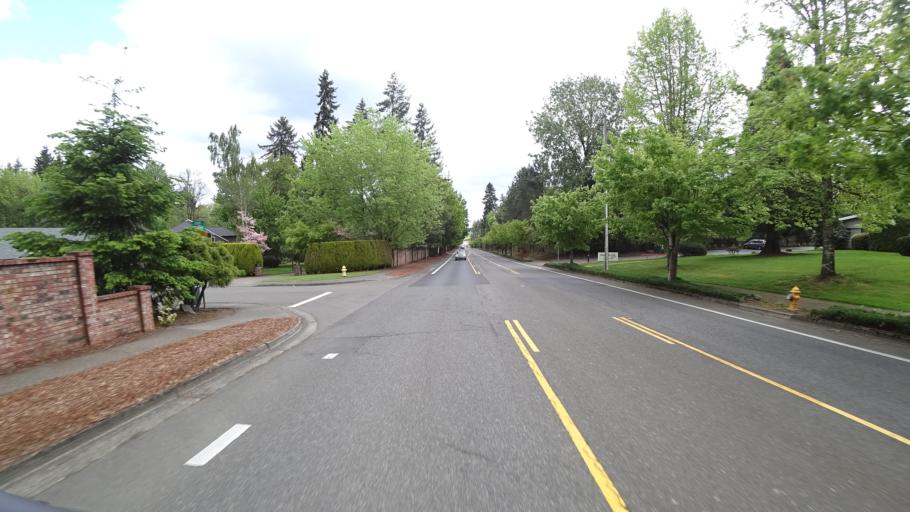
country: US
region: Oregon
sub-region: Washington County
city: Beaverton
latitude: 45.4548
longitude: -122.8143
